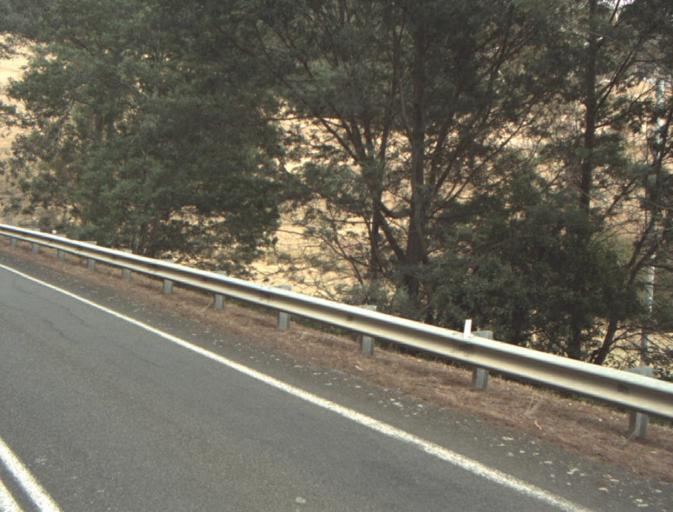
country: AU
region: Tasmania
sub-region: Launceston
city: Mayfield
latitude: -41.2671
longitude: 147.2141
